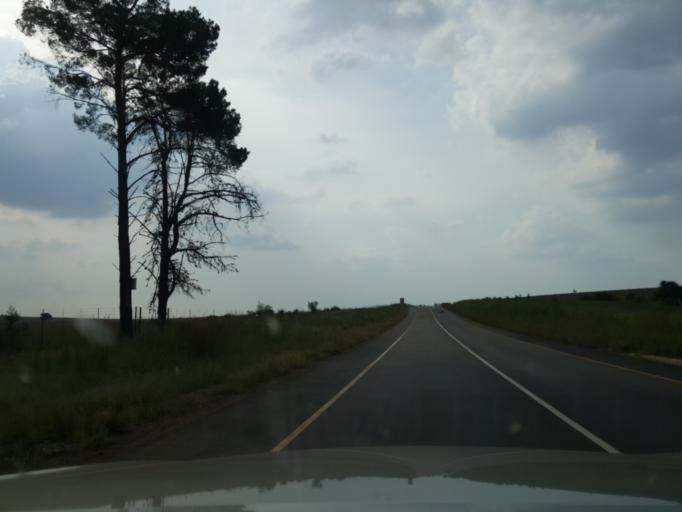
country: ZA
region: Gauteng
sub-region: City of Tshwane Metropolitan Municipality
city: Centurion
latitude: -25.8748
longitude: 28.3110
